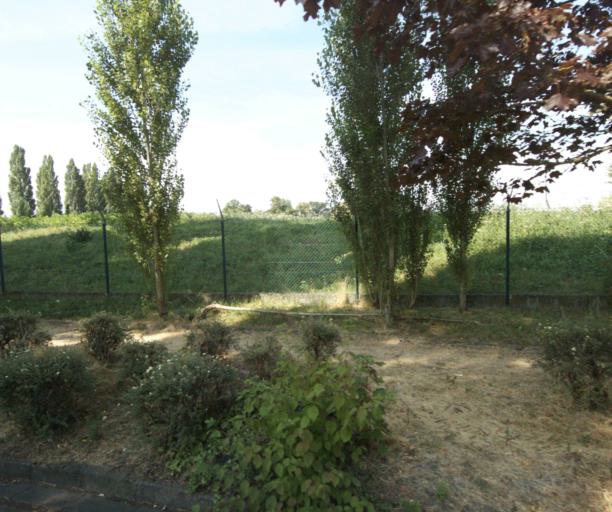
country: FR
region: Nord-Pas-de-Calais
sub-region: Departement du Nord
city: Mouvaux
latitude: 50.7100
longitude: 3.1436
